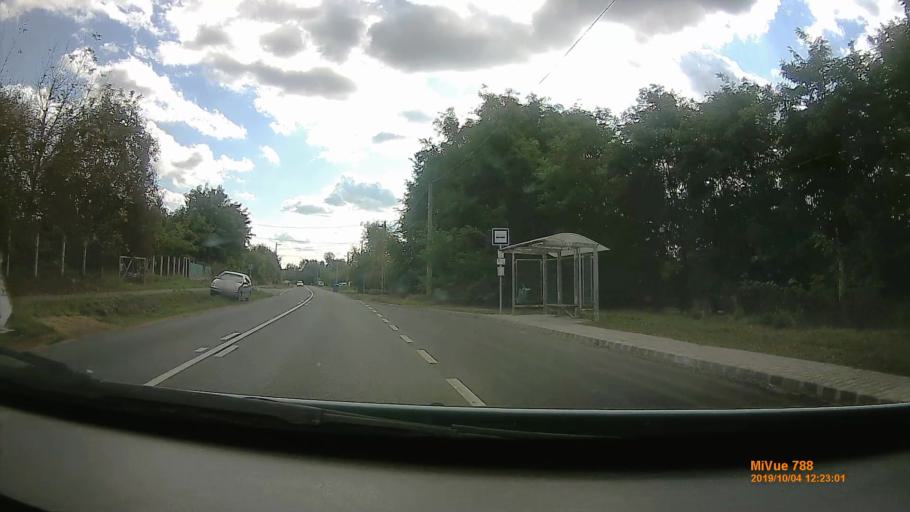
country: HU
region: Szabolcs-Szatmar-Bereg
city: Kotaj
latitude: 48.0086
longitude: 21.6946
